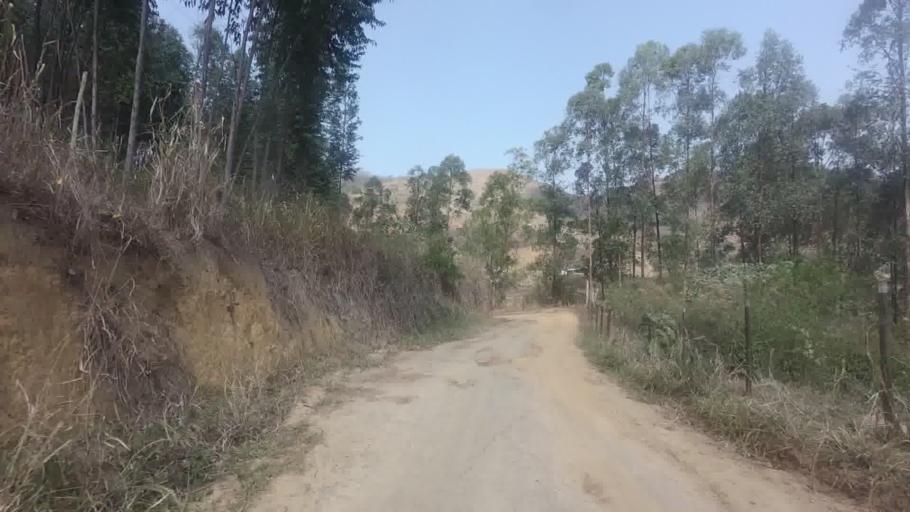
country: BR
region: Espirito Santo
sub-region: Sao Jose Do Calcado
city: Sao Jose do Calcado
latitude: -21.0444
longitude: -41.5240
